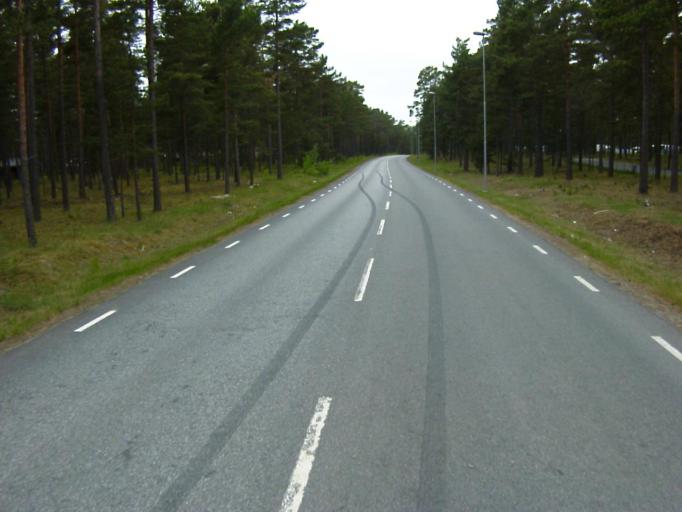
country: SE
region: Skane
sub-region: Kristianstads Kommun
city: Ahus
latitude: 55.9409
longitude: 14.3124
